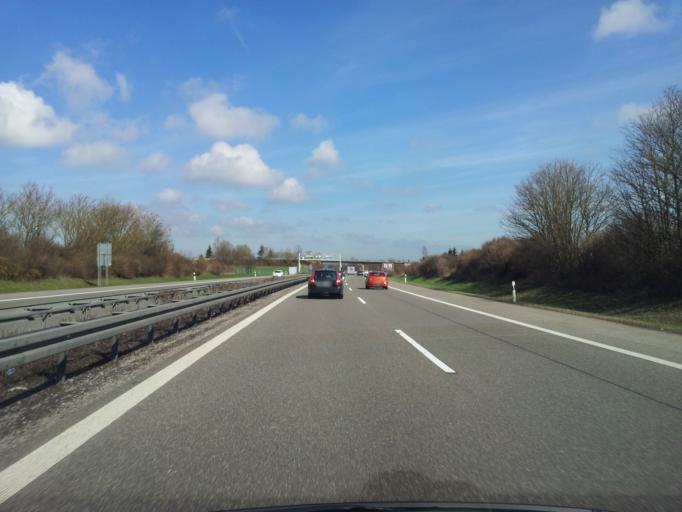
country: DE
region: Baden-Wuerttemberg
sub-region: Freiburg Region
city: Vohringen
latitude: 48.3301
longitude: 8.6465
